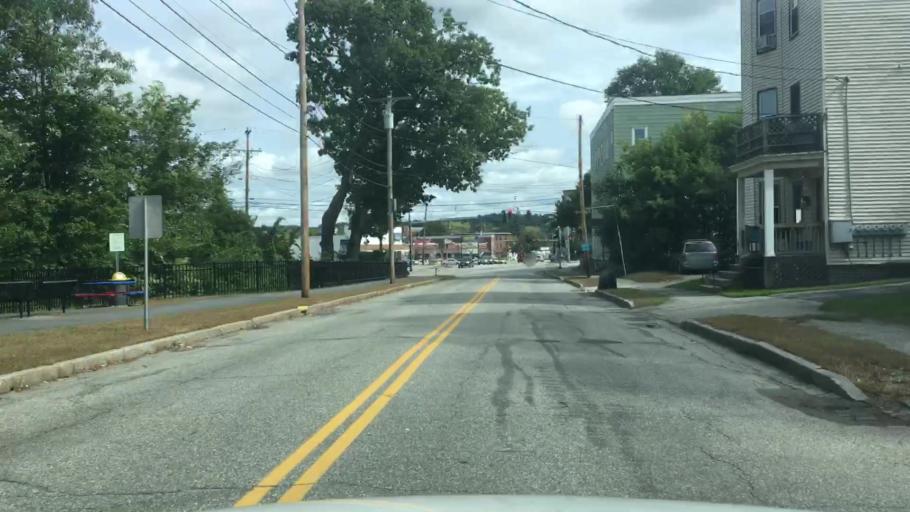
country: US
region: Maine
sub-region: Androscoggin County
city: Auburn
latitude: 44.0876
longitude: -70.2262
